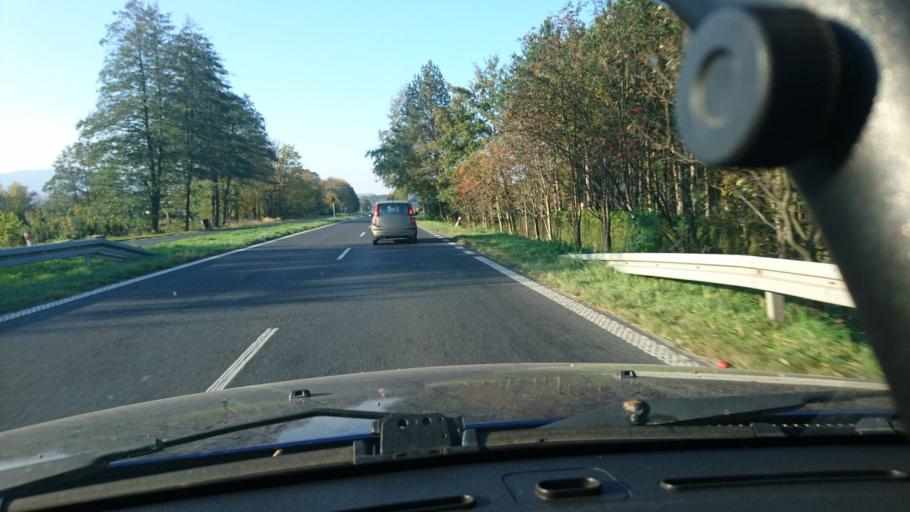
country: PL
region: Silesian Voivodeship
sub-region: Powiat cieszynski
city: Ustron
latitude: 49.7540
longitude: 18.7984
